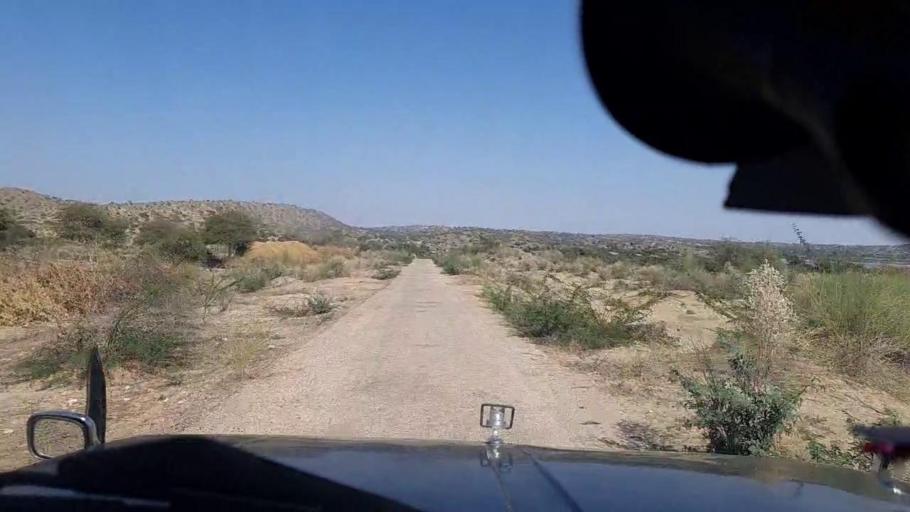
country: PK
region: Sindh
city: Diplo
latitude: 24.4215
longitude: 69.6656
